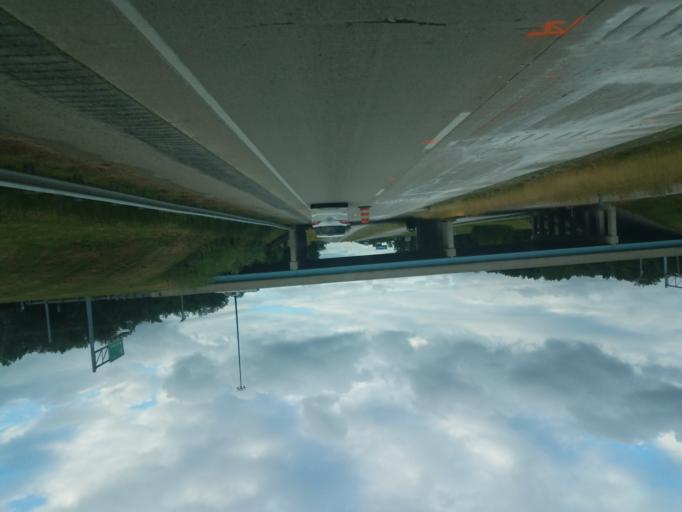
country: US
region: Indiana
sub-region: DeKalb County
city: Waterloo
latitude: 41.4404
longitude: -85.0538
